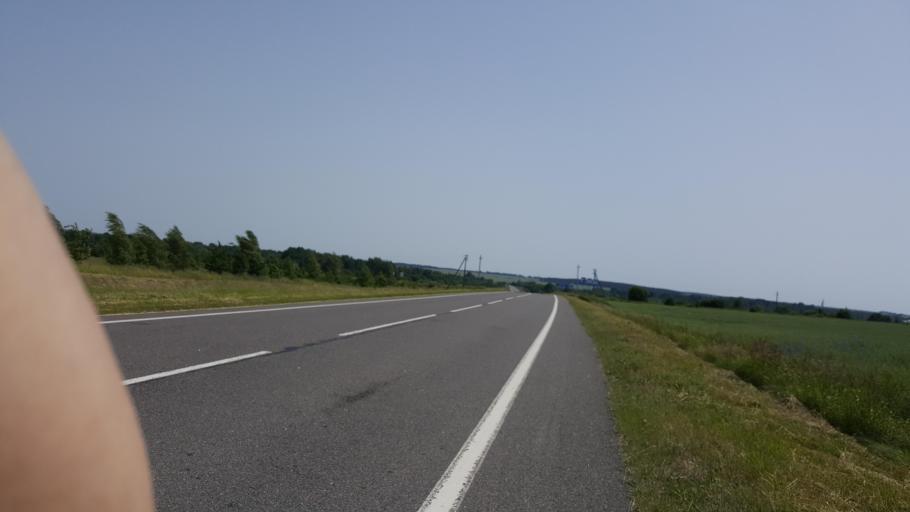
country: BY
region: Brest
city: Kamyanyets
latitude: 52.4350
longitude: 23.8321
